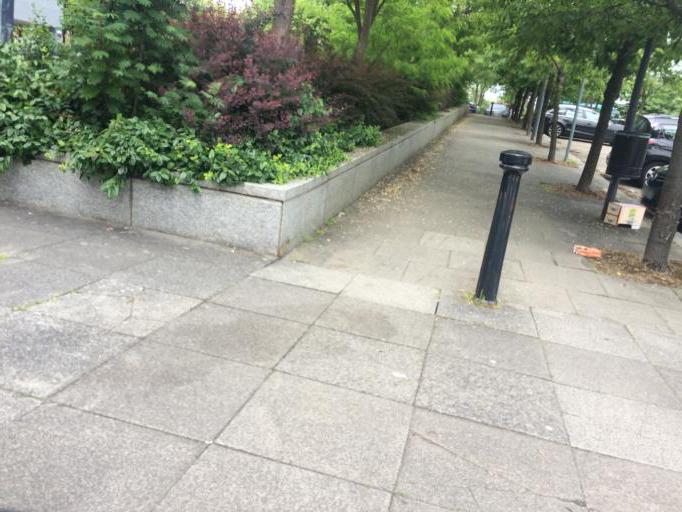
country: GB
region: England
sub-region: Milton Keynes
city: Milton Keynes
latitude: 52.0395
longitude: -0.7593
